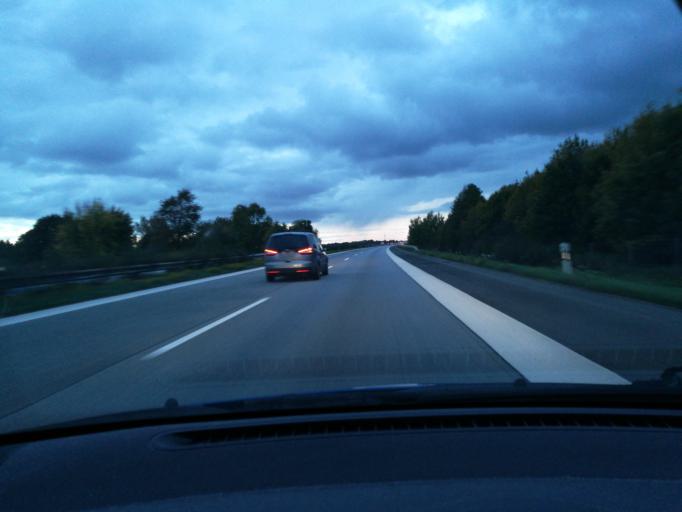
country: DE
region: Schleswig-Holstein
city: Brekendorf
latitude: 54.4266
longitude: 9.5994
